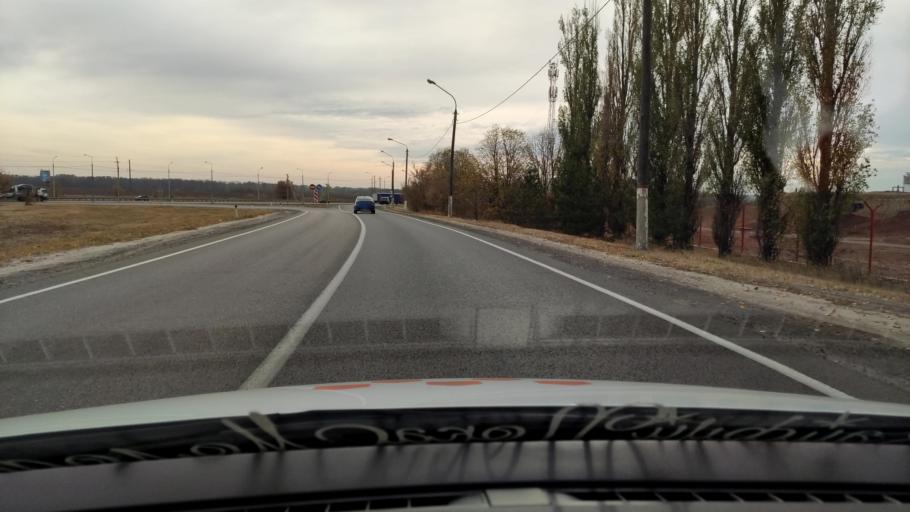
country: RU
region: Voronezj
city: Ramon'
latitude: 51.9287
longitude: 39.2182
